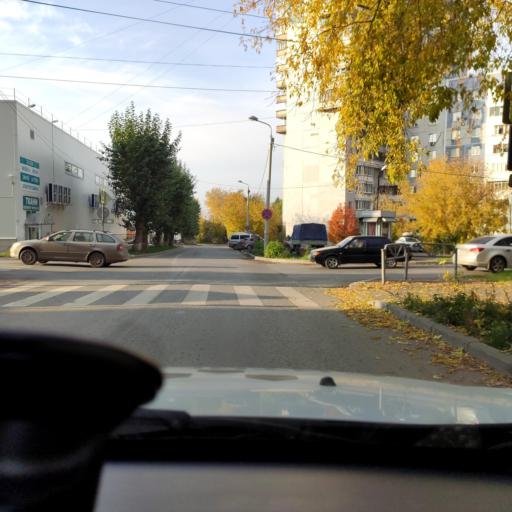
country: RU
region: Perm
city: Perm
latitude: 58.0297
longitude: 56.3046
